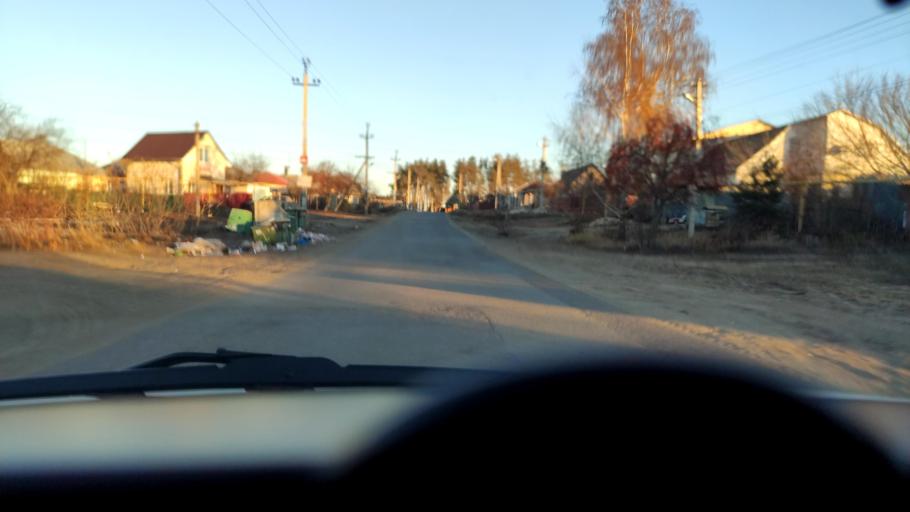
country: RU
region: Voronezj
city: Podgornoye
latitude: 51.7433
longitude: 39.1414
